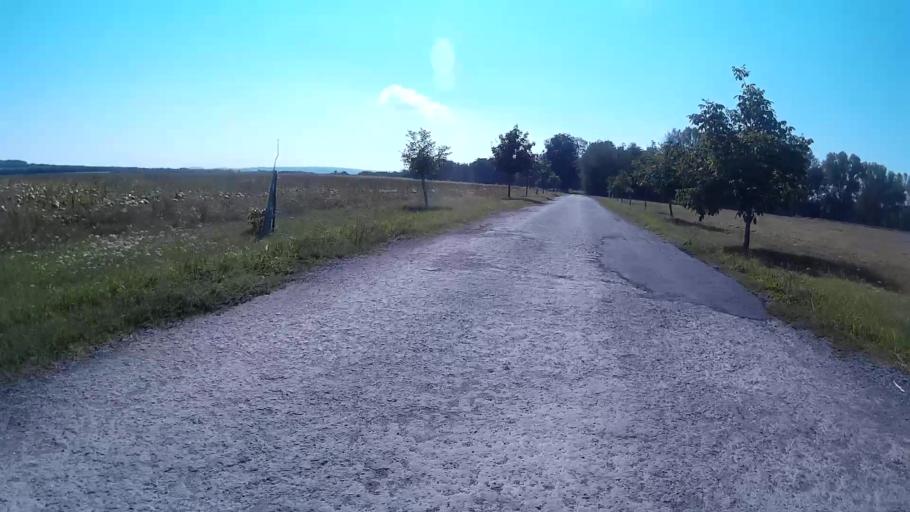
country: CZ
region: South Moravian
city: Novosedly
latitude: 48.8028
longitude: 16.4948
